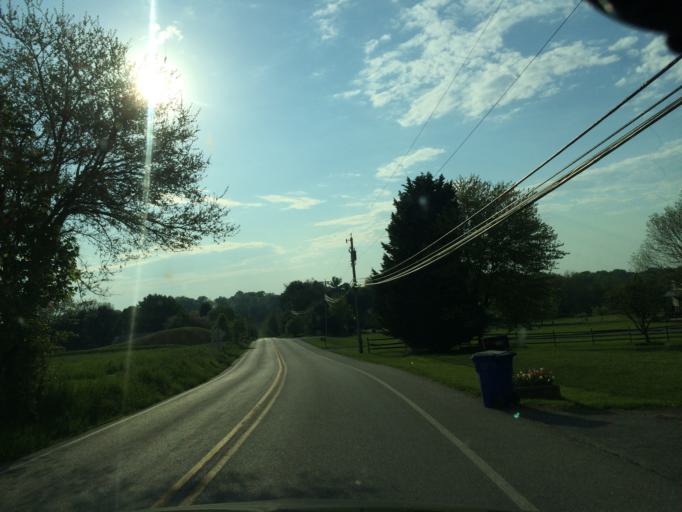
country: US
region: Maryland
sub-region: Howard County
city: Highland
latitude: 39.2152
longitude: -76.9753
